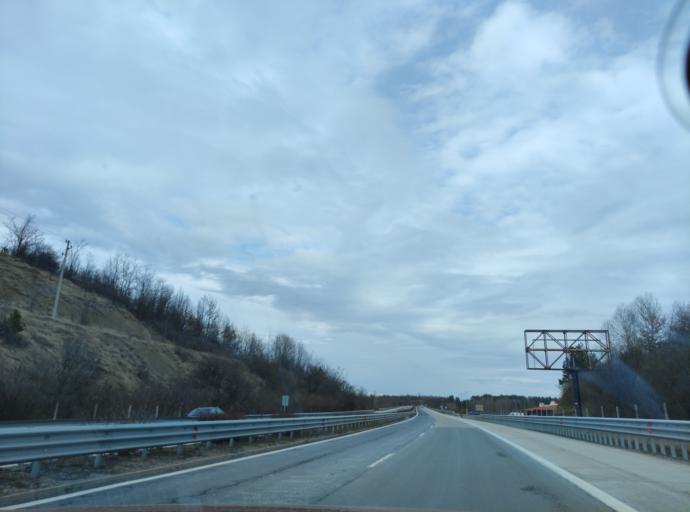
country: BG
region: Sofiya
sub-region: Obshtina Pravets
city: Pravets
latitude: 42.9440
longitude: 23.9884
